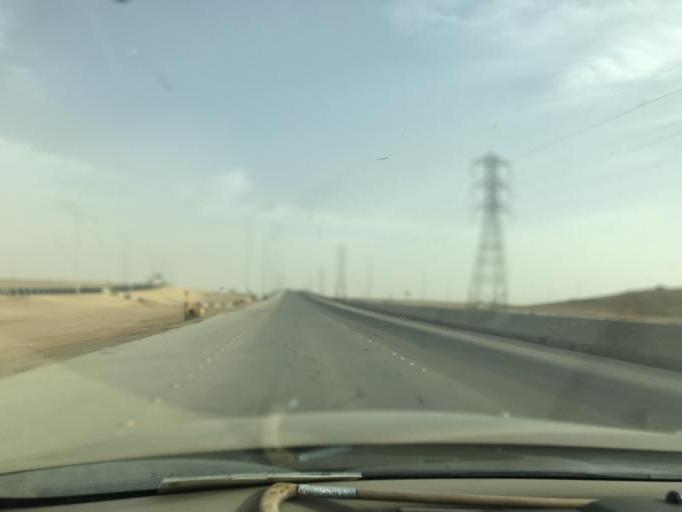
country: SA
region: Ar Riyad
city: Riyadh
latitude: 24.9074
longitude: 46.7030
